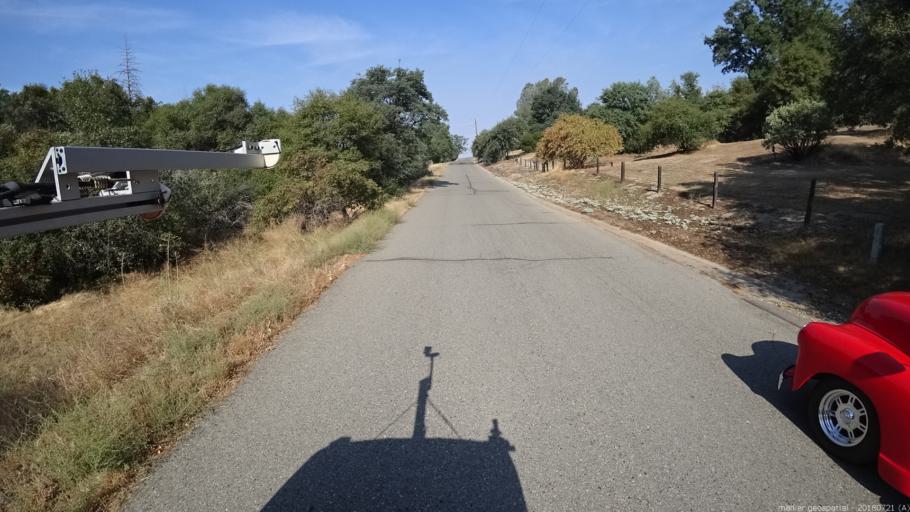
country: US
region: California
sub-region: Fresno County
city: Auberry
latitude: 37.2271
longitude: -119.5255
